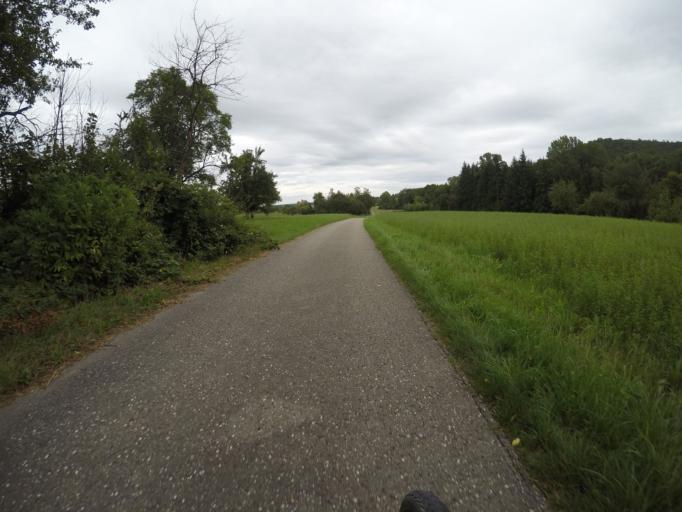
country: DE
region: Baden-Wuerttemberg
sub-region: Regierungsbezirk Stuttgart
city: Nufringen
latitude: 48.6164
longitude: 8.9128
